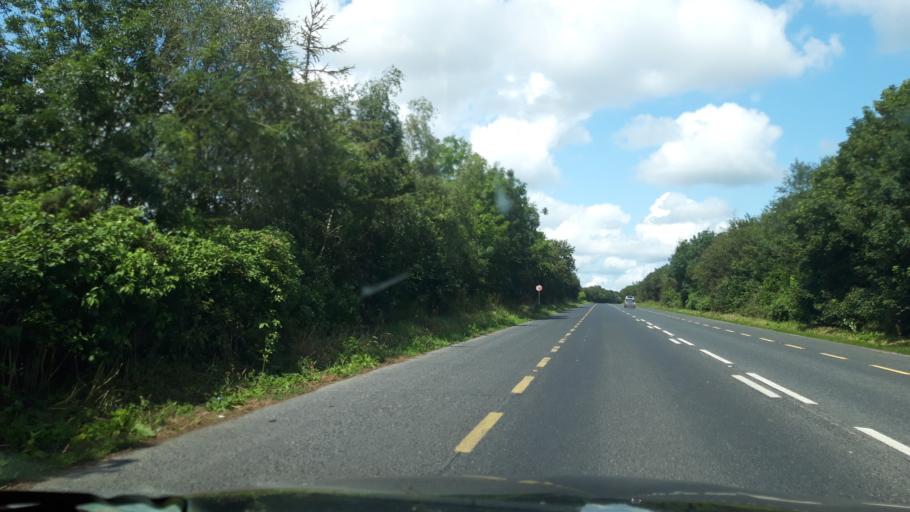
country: IE
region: Munster
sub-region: Waterford
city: Waterford
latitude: 52.2729
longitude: -7.0489
